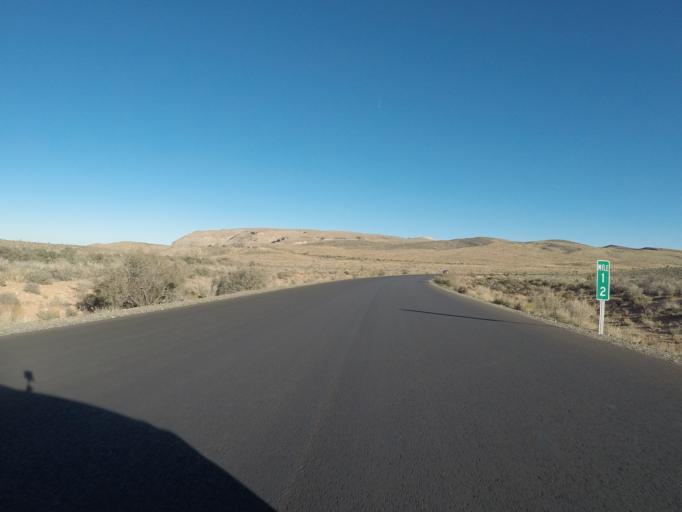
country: US
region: Nevada
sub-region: Clark County
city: Summerlin South
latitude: 36.1159
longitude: -115.4532
